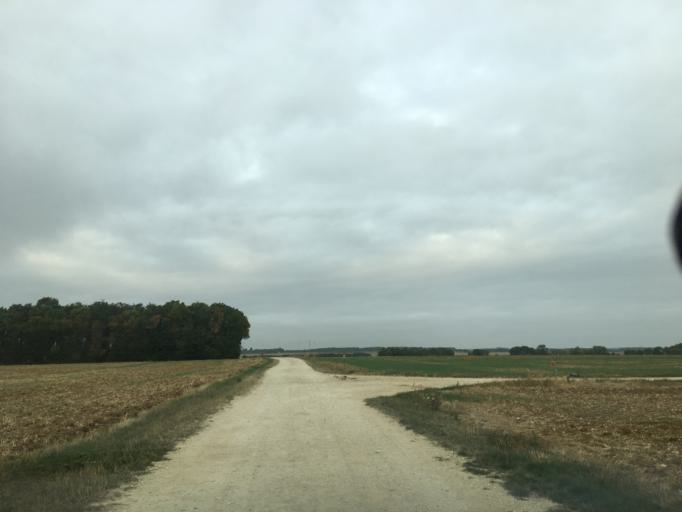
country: FR
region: Poitou-Charentes
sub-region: Departement des Deux-Sevres
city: Beauvoir-sur-Niort
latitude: 46.0890
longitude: -0.5090
